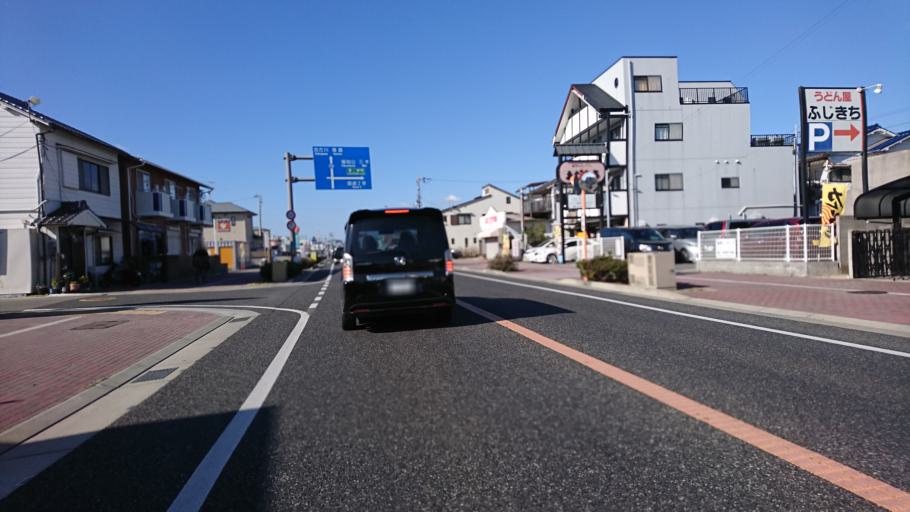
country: JP
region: Hyogo
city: Akashi
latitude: 34.6489
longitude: 134.9746
